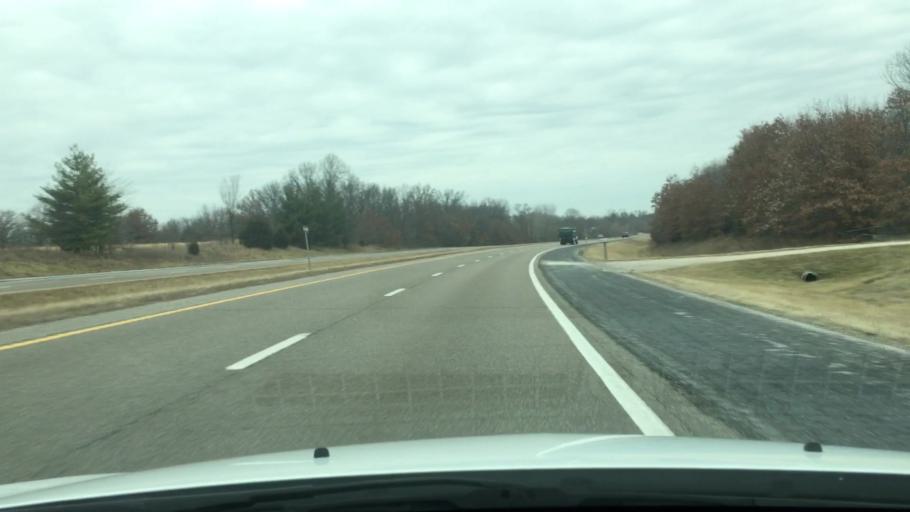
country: US
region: Missouri
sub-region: Audrain County
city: Mexico
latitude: 39.0411
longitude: -91.8929
